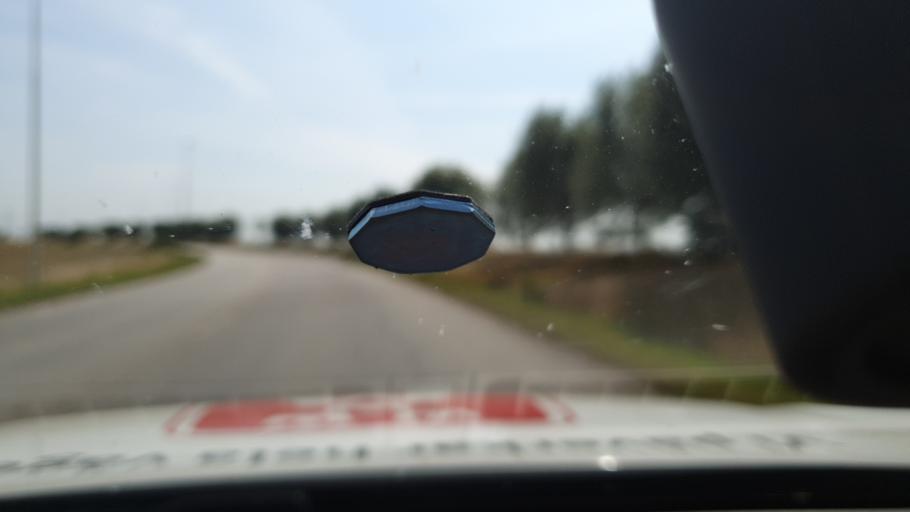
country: SE
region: Skane
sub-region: Burlovs Kommun
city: Arloev
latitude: 55.6321
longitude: 13.0988
